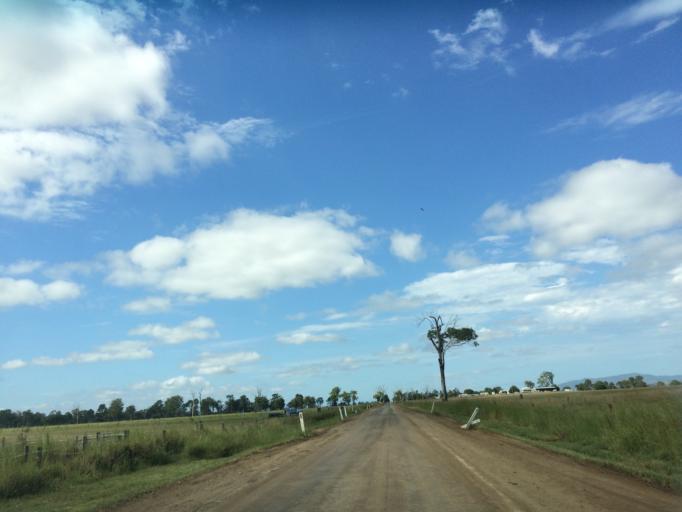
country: AU
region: Queensland
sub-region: Logan
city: Cedar Vale
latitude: -27.8718
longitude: 152.9568
